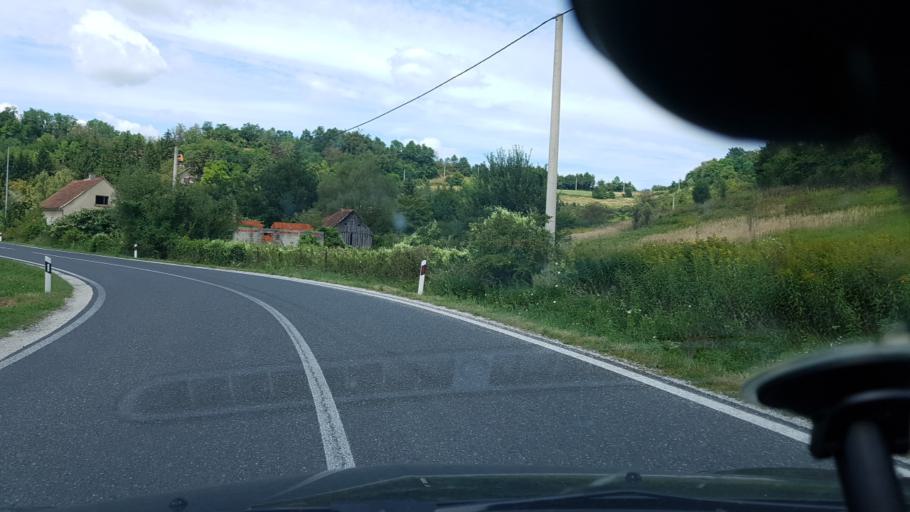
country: HR
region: Varazdinska
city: Lepoglava
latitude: 46.2283
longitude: 15.9934
